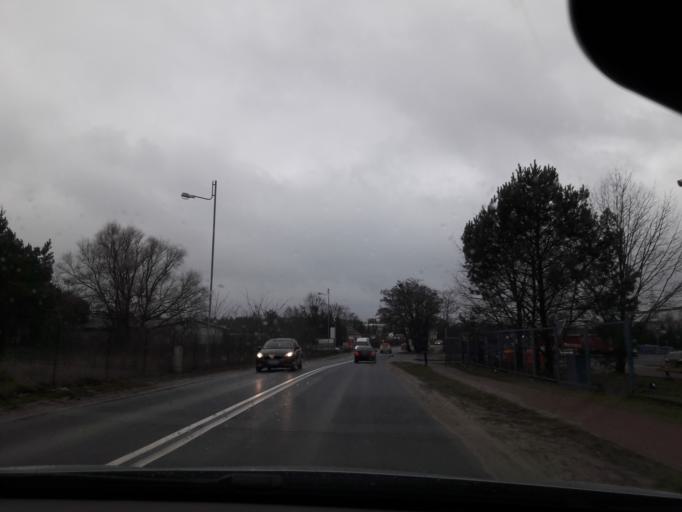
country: PL
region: Greater Poland Voivodeship
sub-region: Powiat poznanski
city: Suchy Las
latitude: 52.4685
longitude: 16.8735
